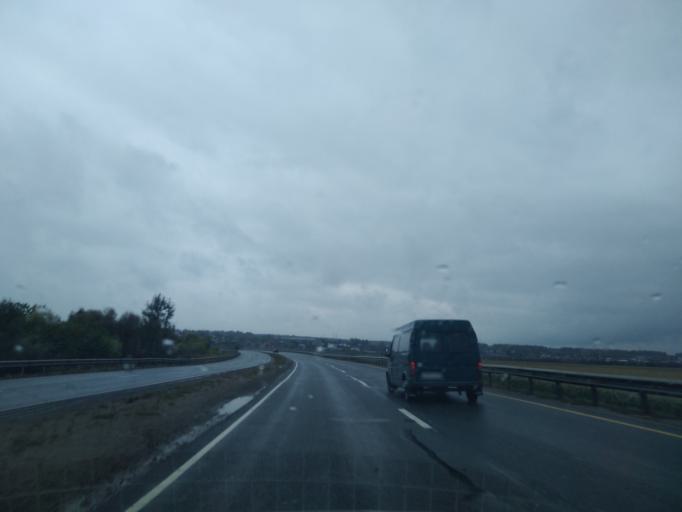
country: RU
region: Tula
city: Barsuki
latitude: 54.2286
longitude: 37.4891
